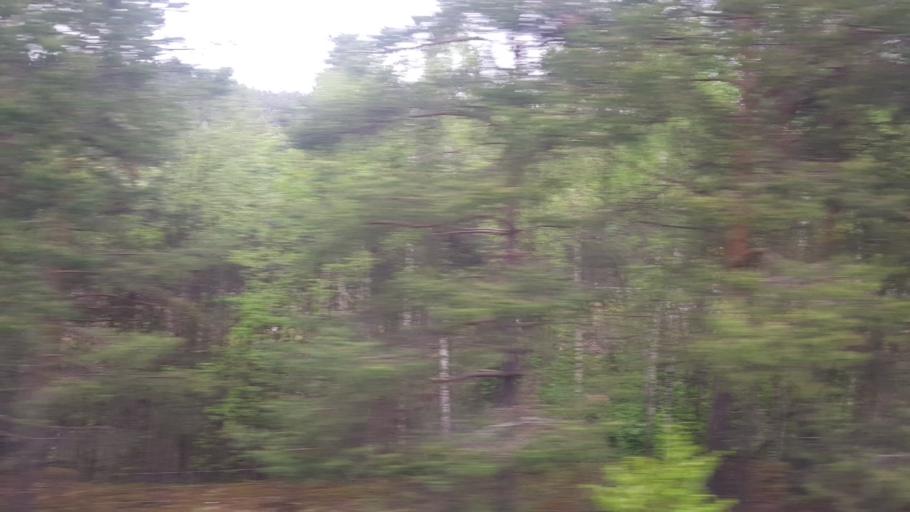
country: NO
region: Oppland
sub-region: Ringebu
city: Ringebu
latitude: 61.5491
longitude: 10.0462
